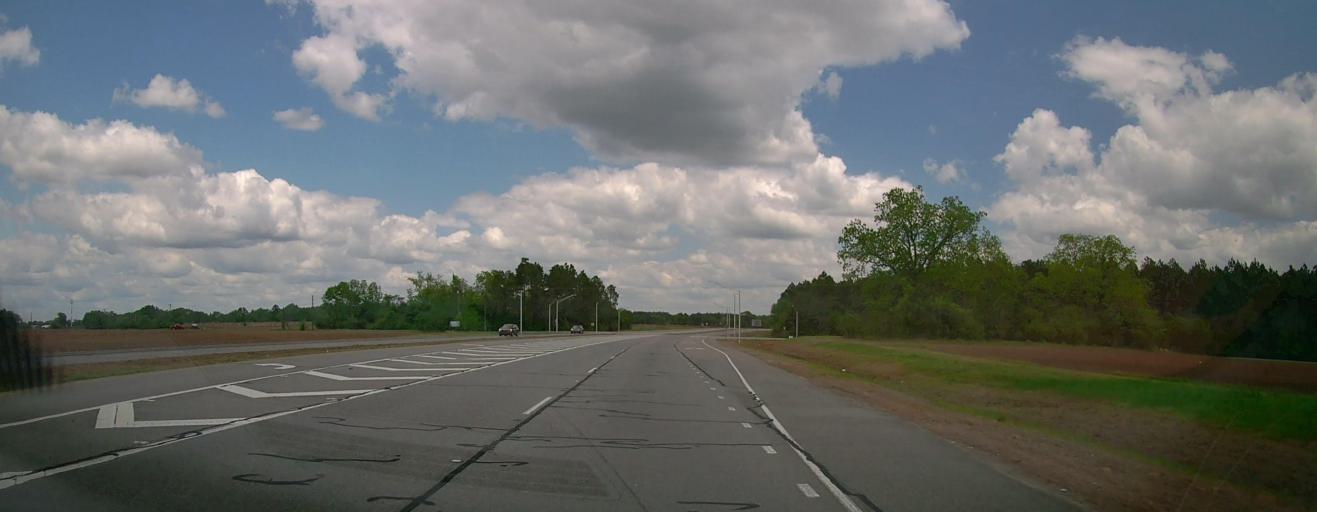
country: US
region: Georgia
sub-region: Laurens County
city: Dublin
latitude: 32.5548
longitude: -82.9774
